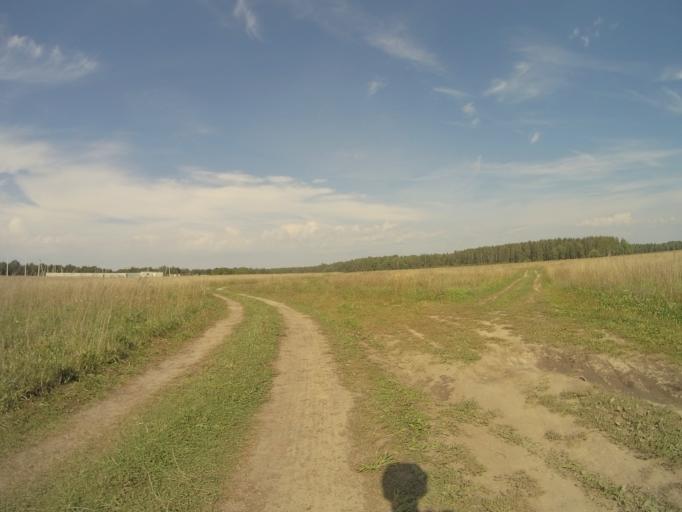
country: RU
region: Vladimir
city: Bogolyubovo
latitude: 56.1144
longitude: 40.5340
